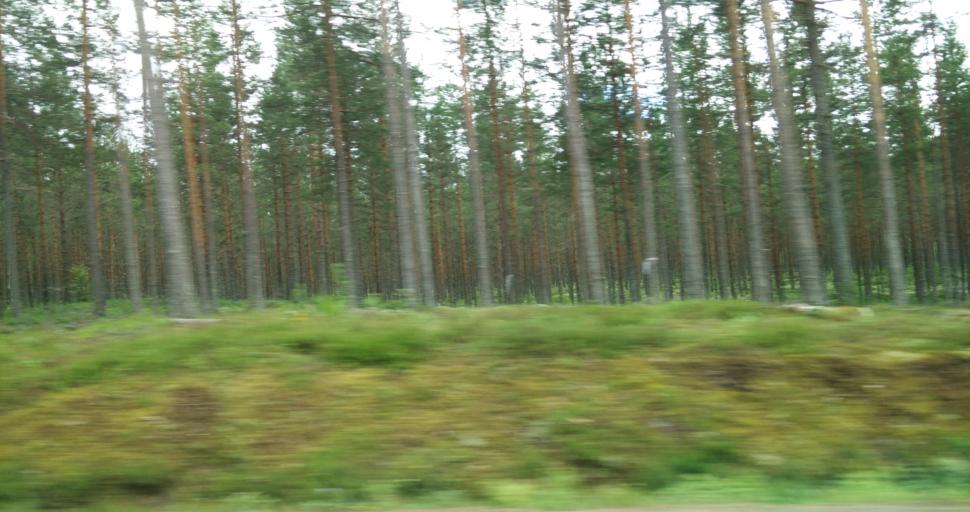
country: SE
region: Vaermland
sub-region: Munkfors Kommun
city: Munkfors
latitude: 59.9685
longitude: 13.5024
